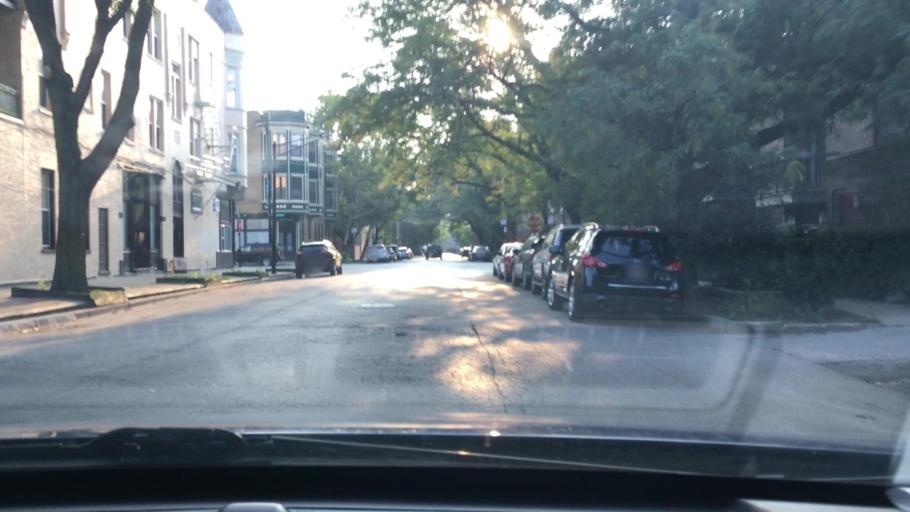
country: US
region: Illinois
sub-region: Cook County
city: Chicago
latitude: 41.9199
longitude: -87.6576
